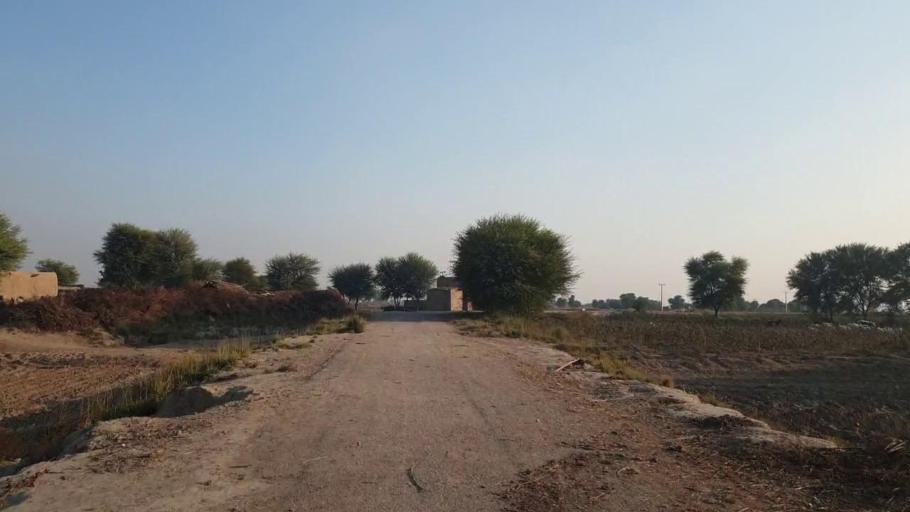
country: PK
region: Sindh
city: Sehwan
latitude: 26.4508
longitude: 67.7836
